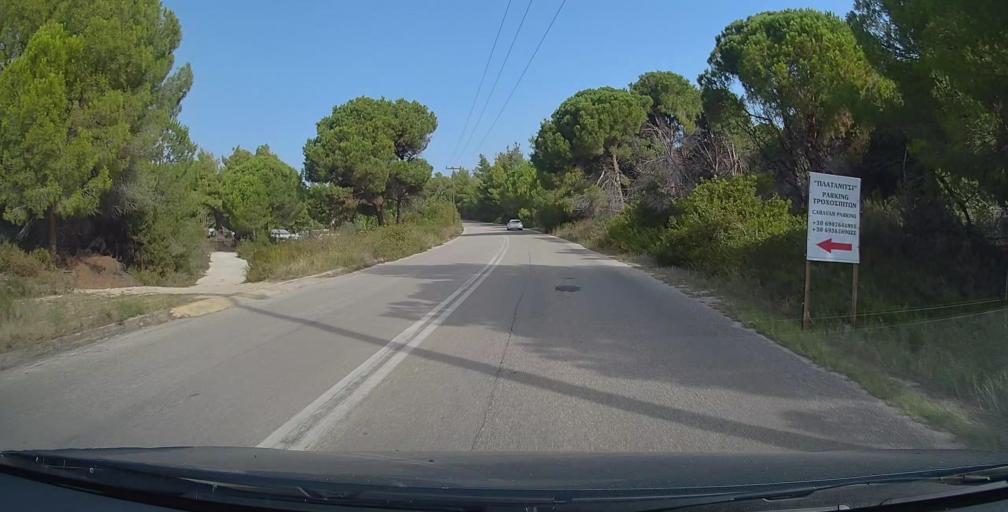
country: GR
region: Central Macedonia
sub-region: Nomos Chalkidikis
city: Sarti
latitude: 40.1195
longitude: 23.9706
